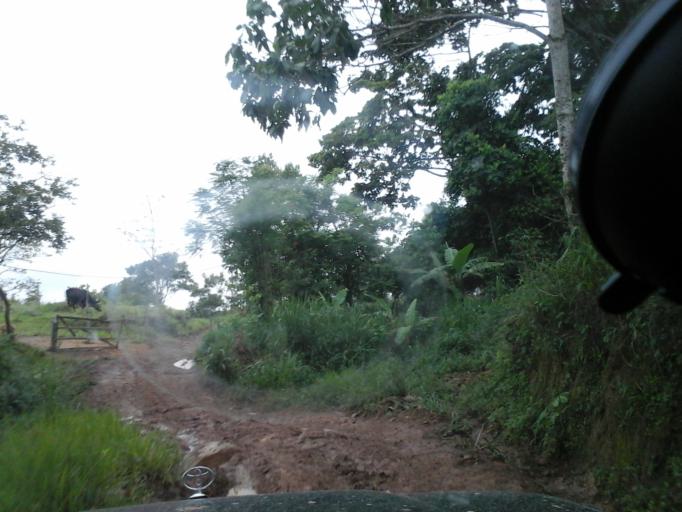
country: CO
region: Cesar
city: Agustin Codazzi
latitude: 9.9573
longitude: -73.0635
